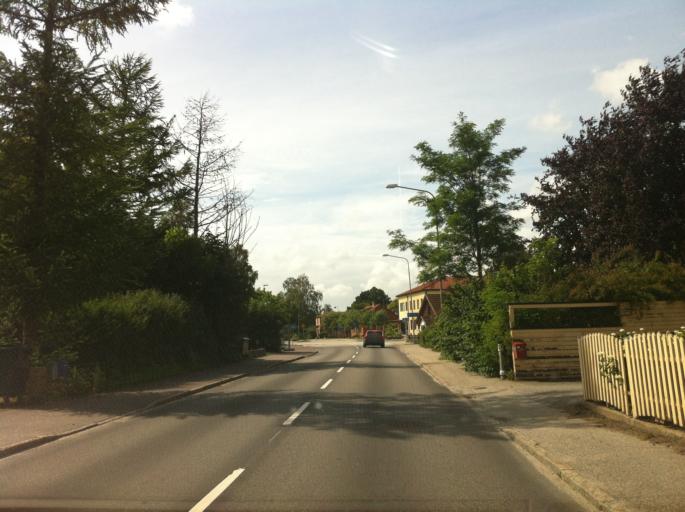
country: SE
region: Skane
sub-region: Trelleborgs Kommun
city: Anderslov
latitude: 55.4903
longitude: 13.3762
